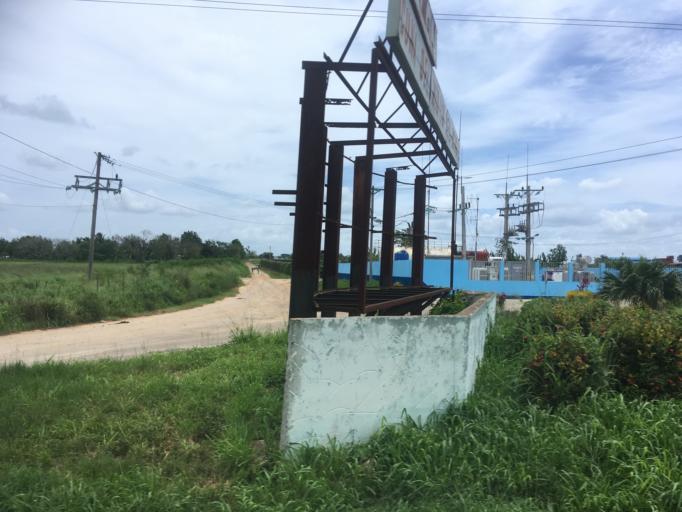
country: CU
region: Matanzas
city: Colon
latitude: 22.7045
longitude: -80.8777
